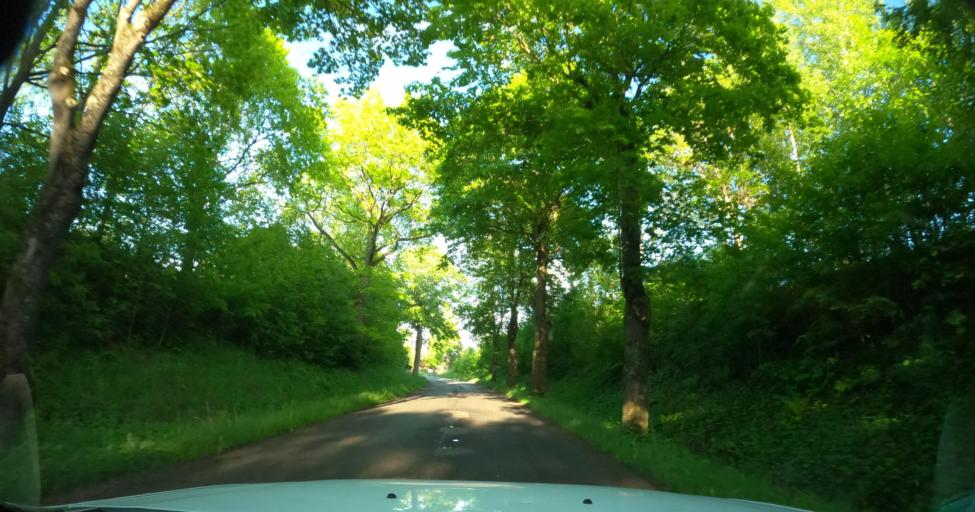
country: PL
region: Warmian-Masurian Voivodeship
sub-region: Powiat braniewski
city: Braniewo
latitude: 54.2810
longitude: 19.8744
